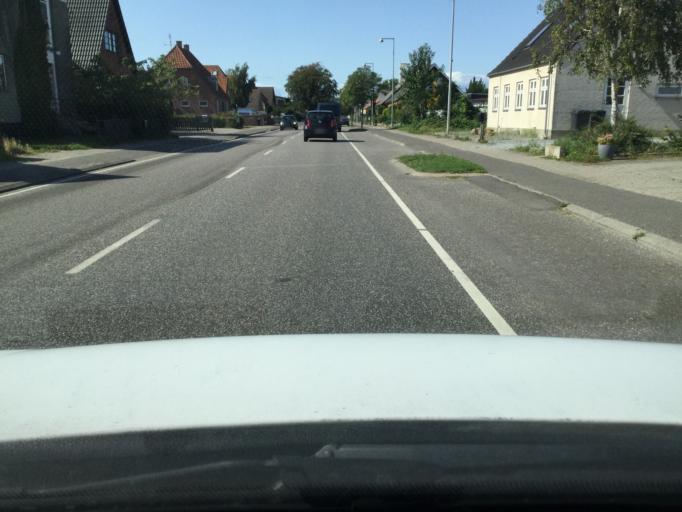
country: DK
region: Zealand
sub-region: Lolland Kommune
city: Nakskov
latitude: 54.8253
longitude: 11.1492
